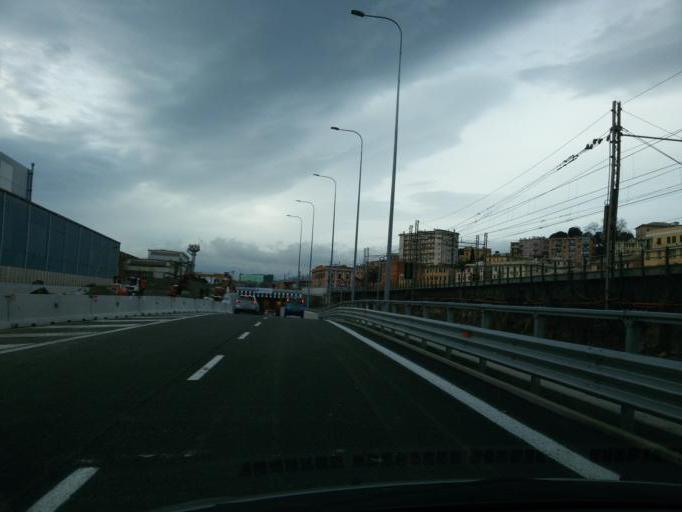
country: IT
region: Liguria
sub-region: Provincia di Genova
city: San Teodoro
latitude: 44.4140
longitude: 8.8679
